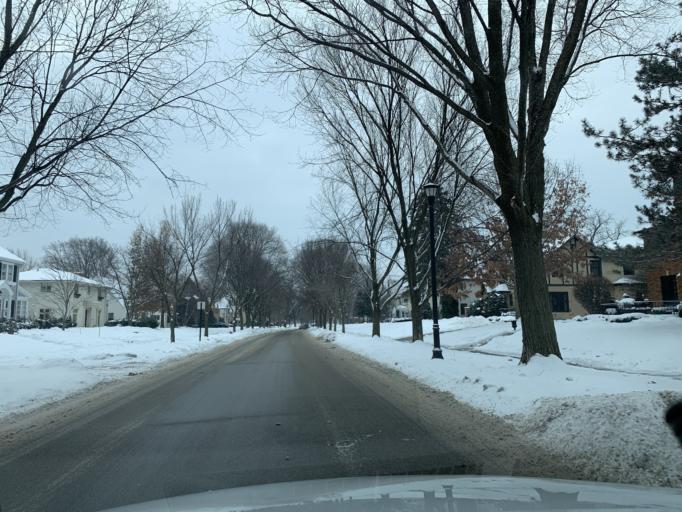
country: US
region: Minnesota
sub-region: Hennepin County
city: Edina
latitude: 44.9184
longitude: -93.3401
